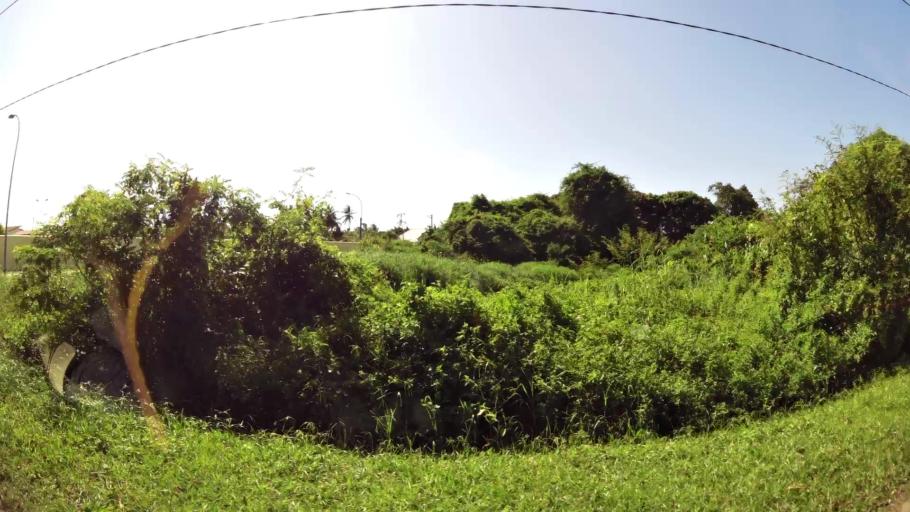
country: GF
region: Guyane
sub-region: Guyane
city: Remire-Montjoly
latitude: 4.9164
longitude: -52.2701
